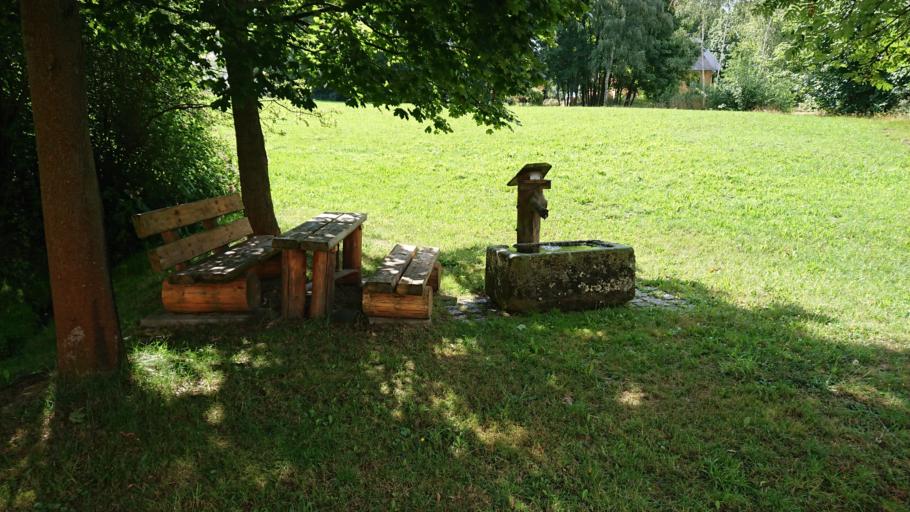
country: DE
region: Bavaria
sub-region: Upper Palatinate
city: Neualbenreuth
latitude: 49.9536
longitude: 12.4650
